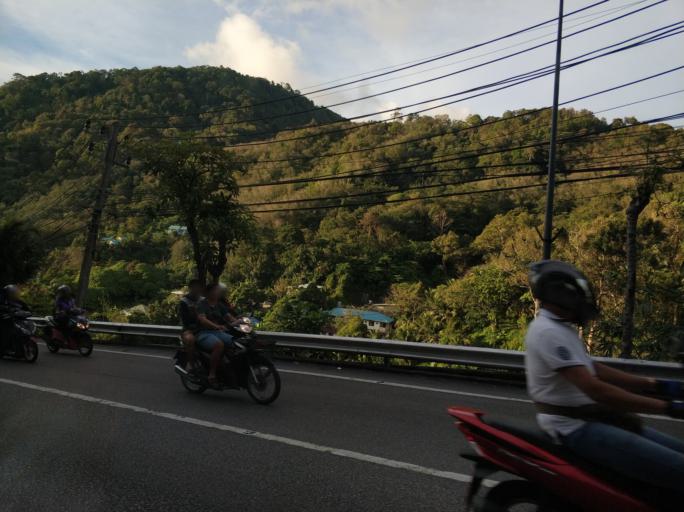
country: TH
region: Phuket
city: Kathu
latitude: 7.9030
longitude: 98.3196
